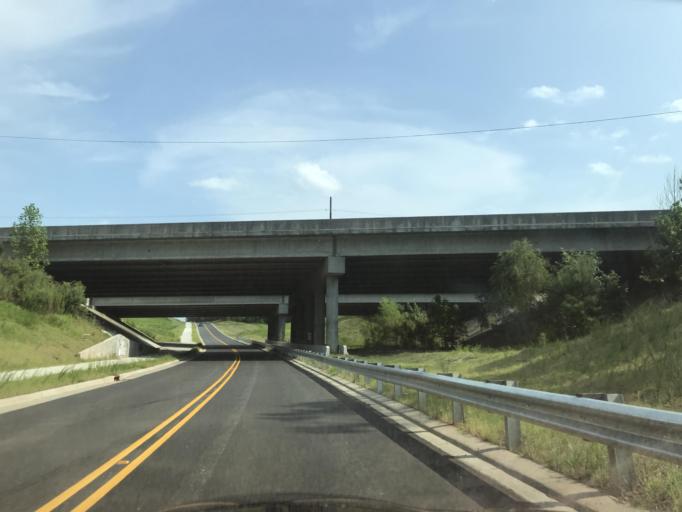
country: US
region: North Carolina
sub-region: Wake County
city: Morrisville
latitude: 35.8454
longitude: -78.8785
